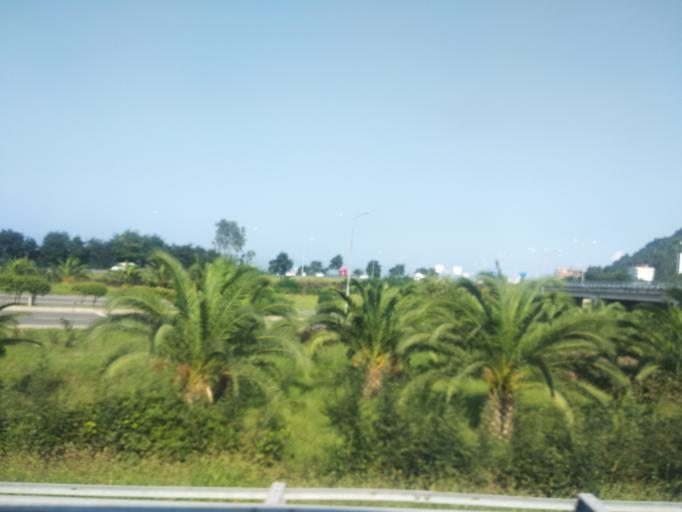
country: TR
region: Ordu
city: Ordu
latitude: 41.0173
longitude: 37.8437
